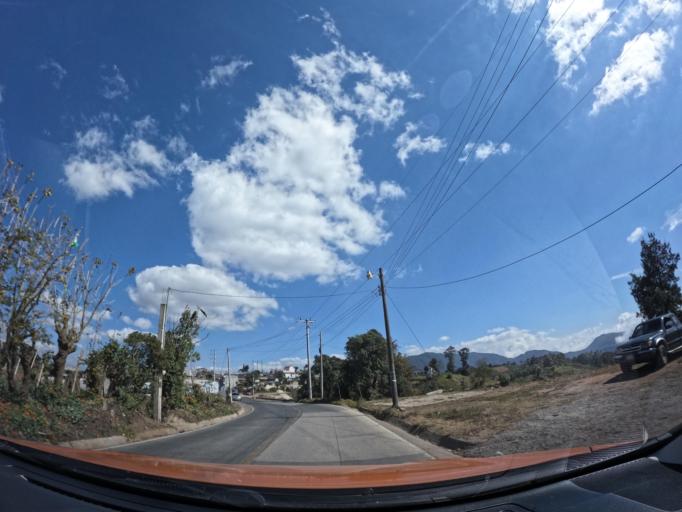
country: GT
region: Chimaltenango
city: Patzun
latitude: 14.6474
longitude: -91.0405
